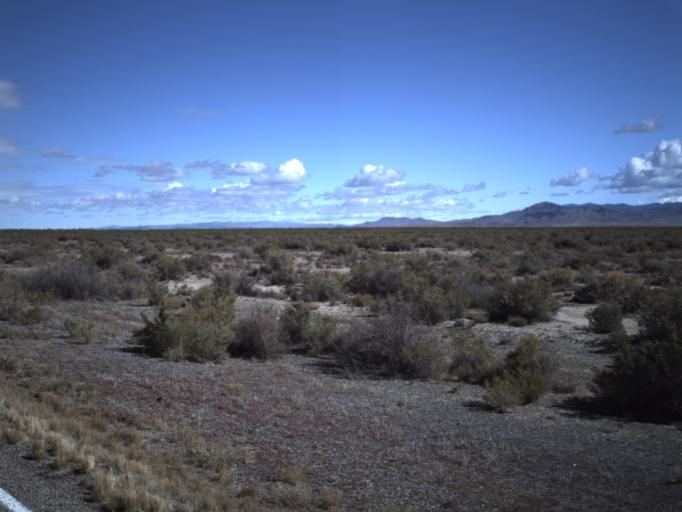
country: US
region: Nevada
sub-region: White Pine County
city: McGill
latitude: 39.0331
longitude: -114.0358
